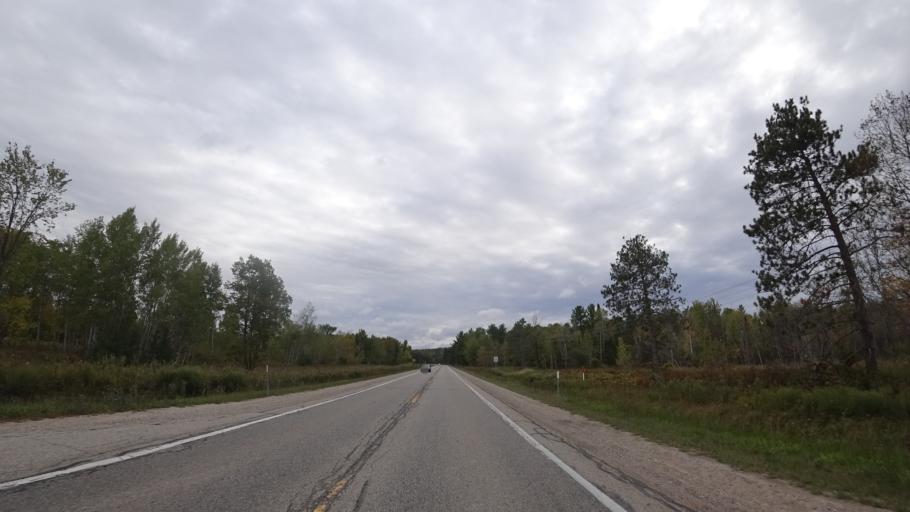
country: US
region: Michigan
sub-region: Charlevoix County
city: Boyne City
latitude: 45.2188
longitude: -84.9234
